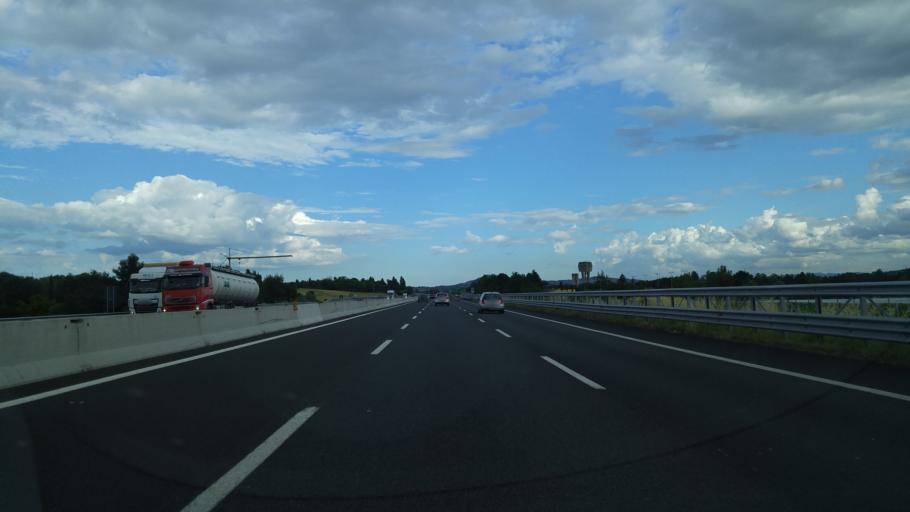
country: IT
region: Emilia-Romagna
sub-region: Provincia di Rimini
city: Santa Monica-Cella
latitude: 43.9609
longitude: 12.6971
